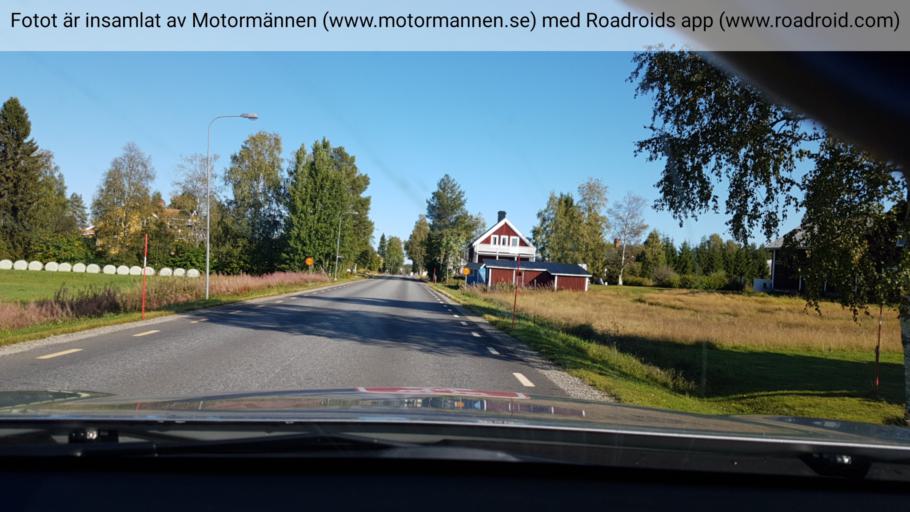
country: SE
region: Vaesterbotten
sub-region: Norsjo Kommun
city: Norsjoe
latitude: 64.5226
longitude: 19.3473
